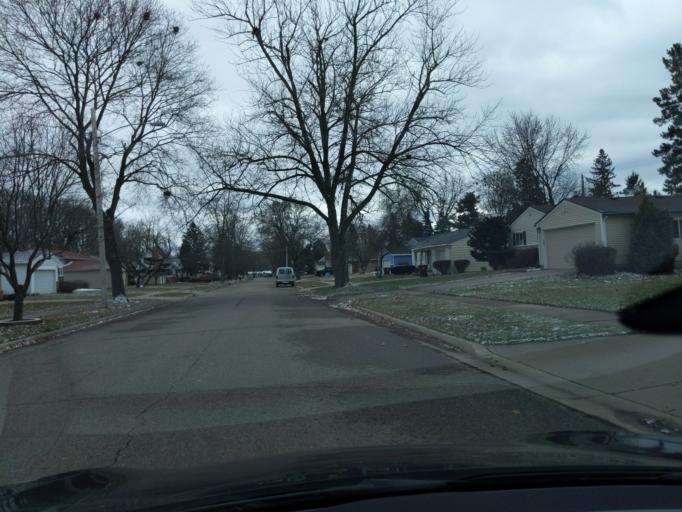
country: US
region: Michigan
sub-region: Ingham County
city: East Lansing
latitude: 42.7534
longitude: -84.5138
